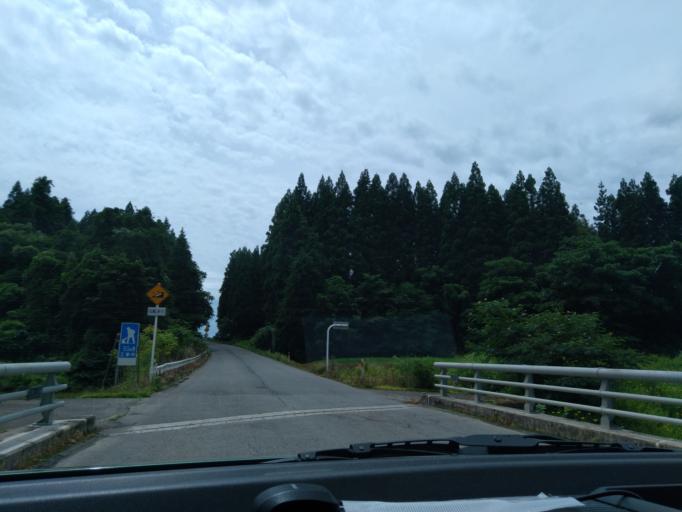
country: JP
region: Akita
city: Kakunodatemachi
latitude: 39.5893
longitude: 140.6194
